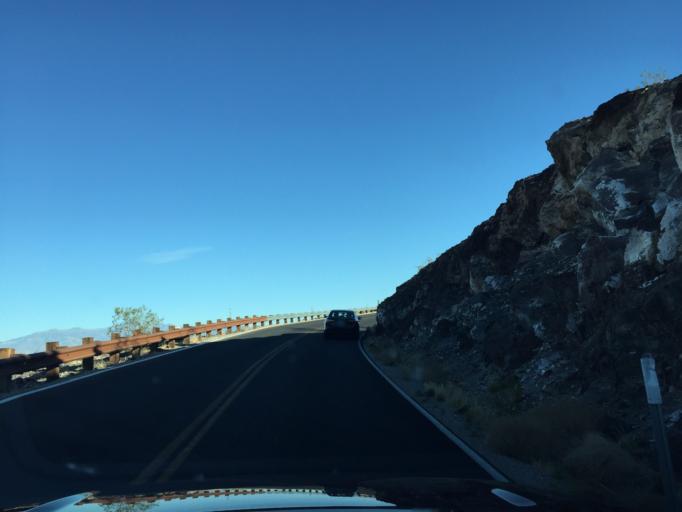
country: US
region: California
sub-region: Inyo County
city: Lone Pine
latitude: 36.3551
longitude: -117.5351
